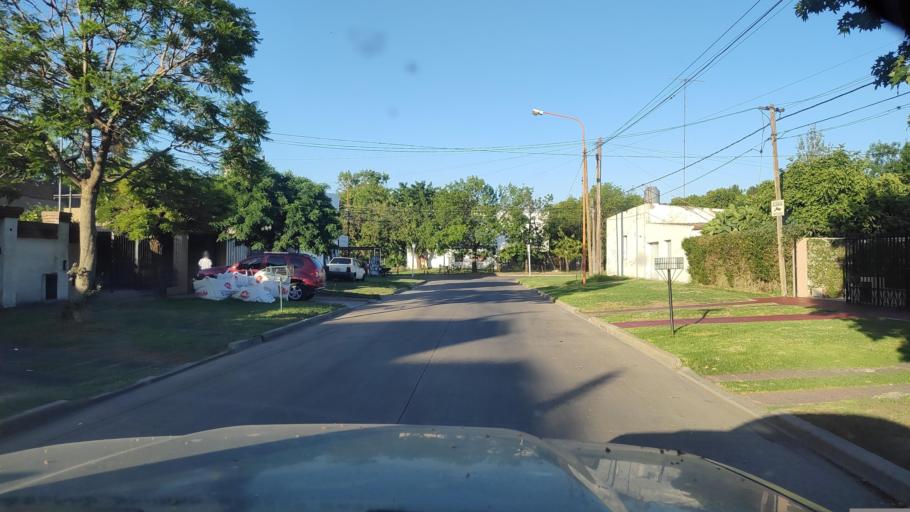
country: AR
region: Buenos Aires
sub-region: Partido de Lujan
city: Lujan
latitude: -34.5761
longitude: -59.1100
